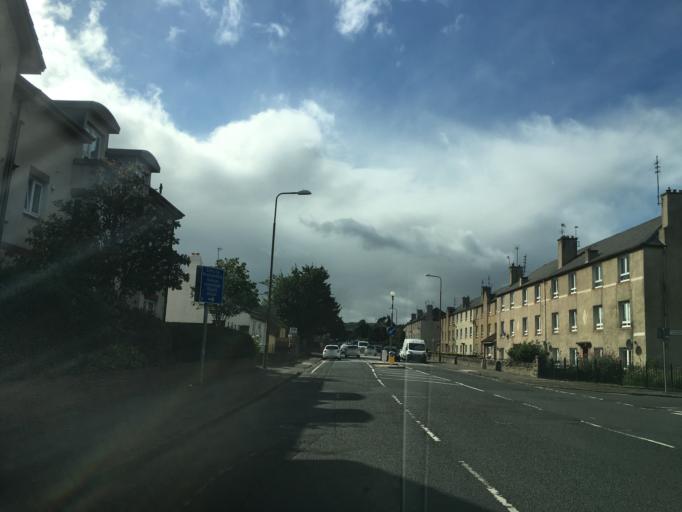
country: GB
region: Scotland
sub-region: West Lothian
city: Seafield
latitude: 55.9321
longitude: -3.1550
